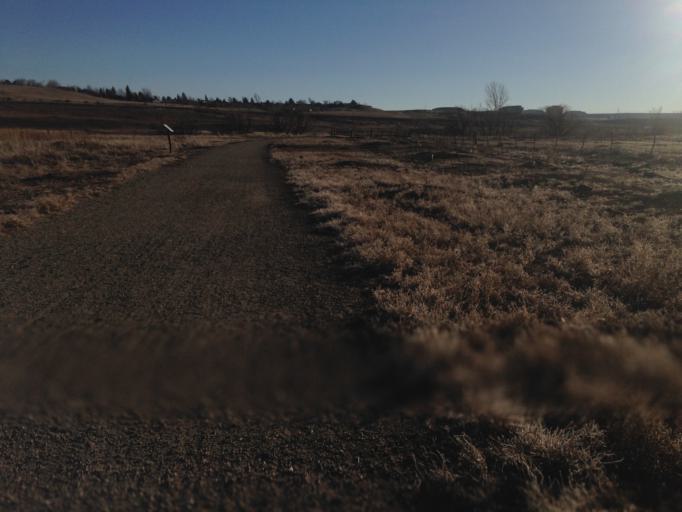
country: US
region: Colorado
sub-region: Broomfield County
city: Broomfield
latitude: 39.9393
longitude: -105.1092
